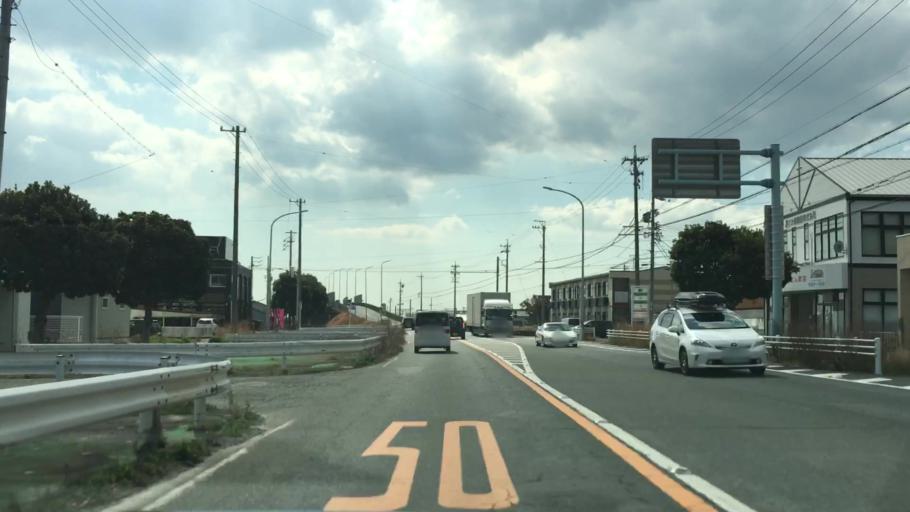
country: JP
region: Aichi
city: Kozakai-cho
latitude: 34.8156
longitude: 137.3154
